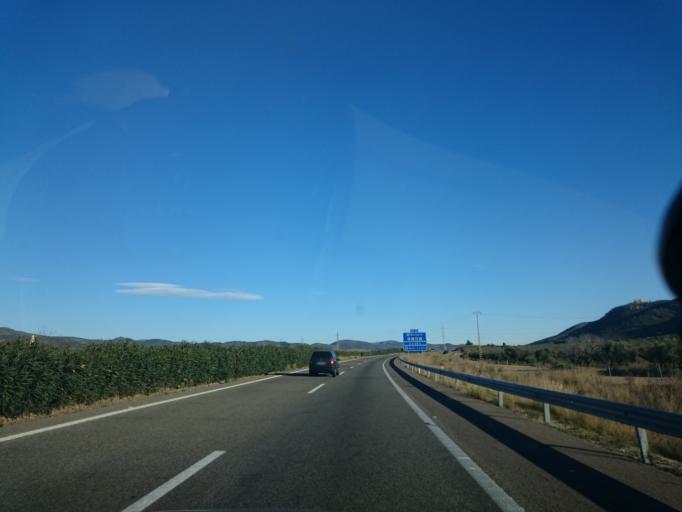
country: ES
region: Valencia
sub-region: Provincia de Castello
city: Alcala de Xivert
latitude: 40.2913
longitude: 0.2296
